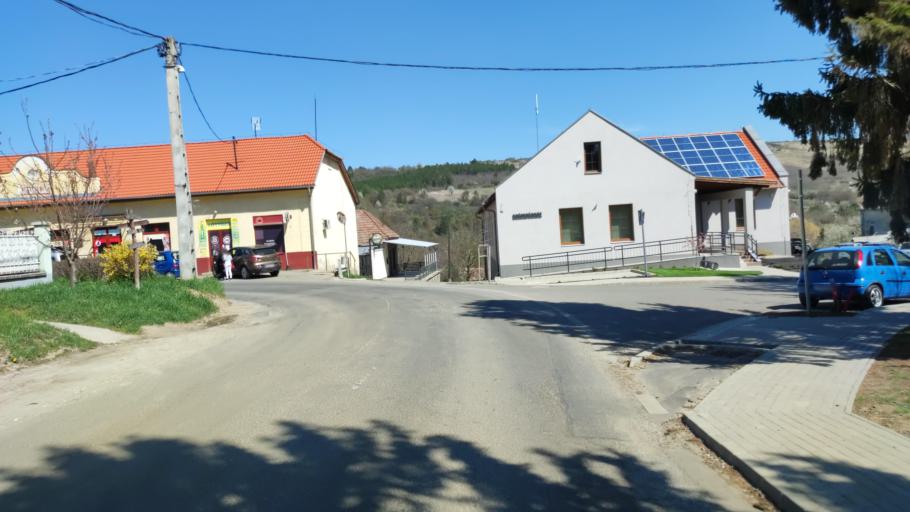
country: HU
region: Pest
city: Kosd
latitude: 47.8016
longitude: 19.1776
